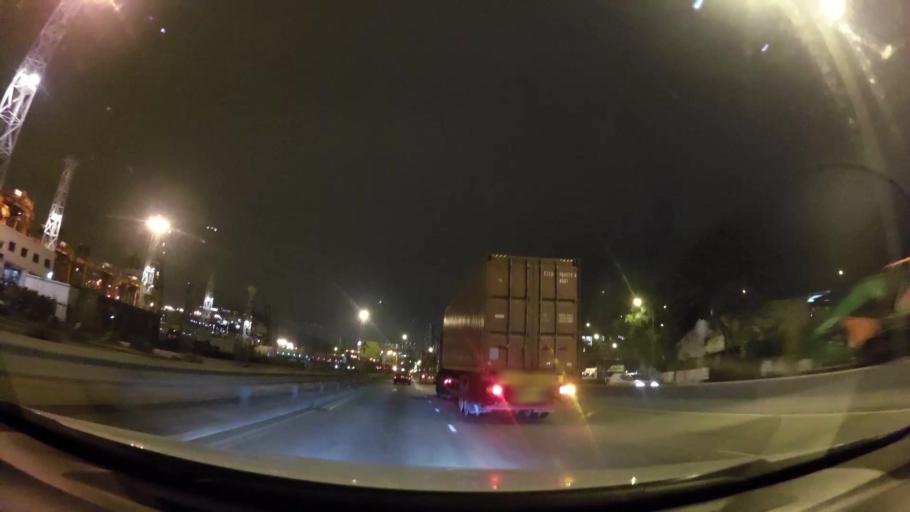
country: HK
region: Sham Shui Po
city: Sham Shui Po
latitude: 22.3351
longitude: 114.1322
